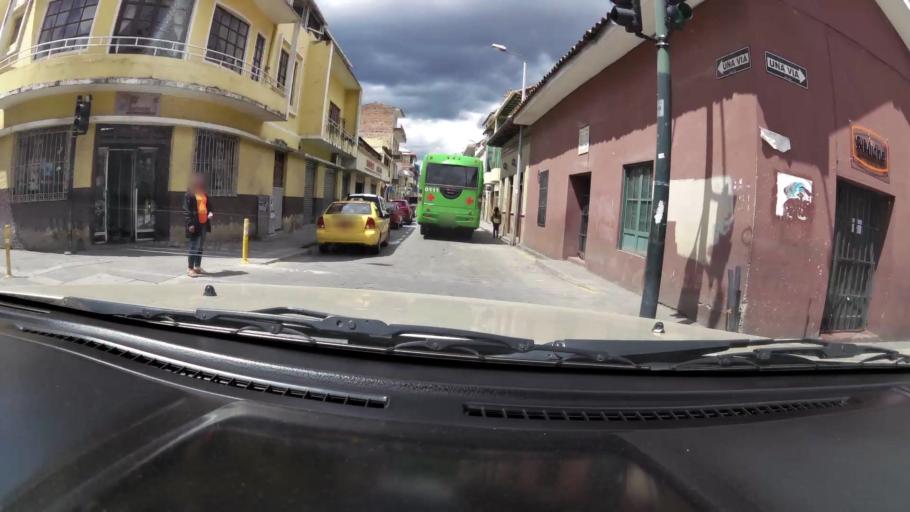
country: EC
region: Azuay
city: Cuenca
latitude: -2.8970
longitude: -78.9998
